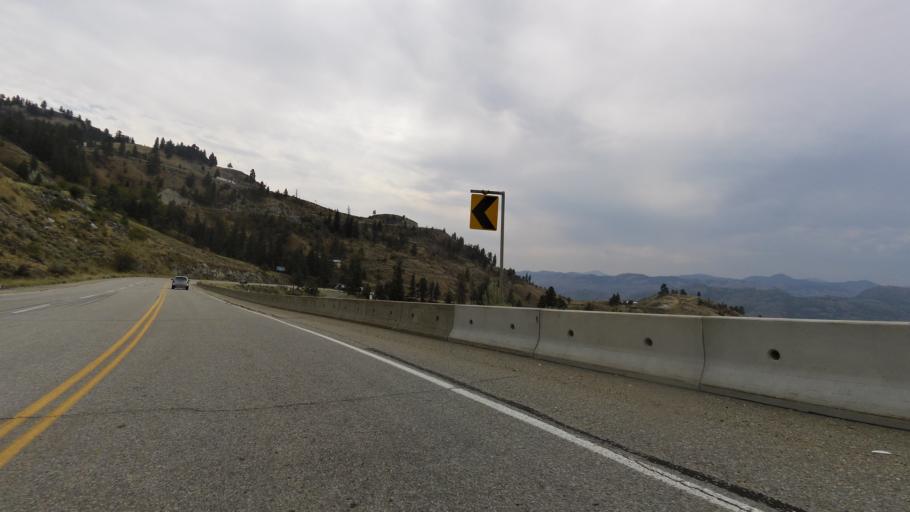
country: CA
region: British Columbia
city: Osoyoos
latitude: 49.0176
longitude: -119.4041
